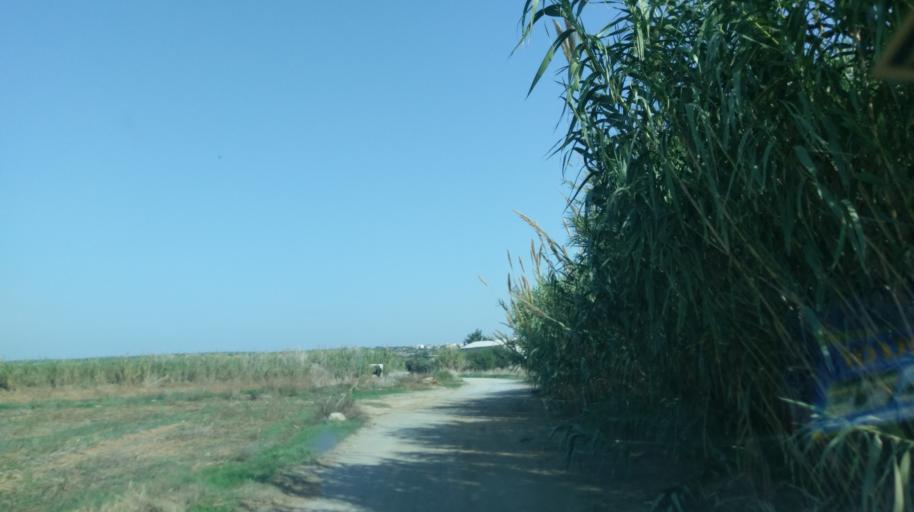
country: CY
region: Lefkosia
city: Morfou
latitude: 35.2926
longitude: 32.9518
